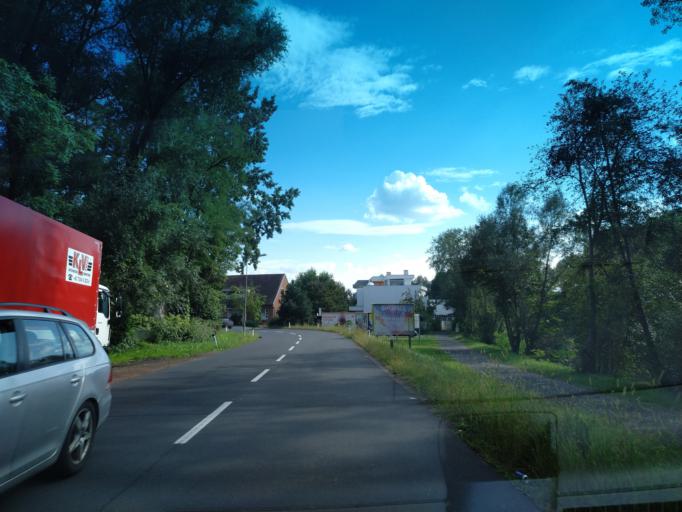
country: AT
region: Styria
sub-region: Politischer Bezirk Leibnitz
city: Kaindorf an der Sulm
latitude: 46.7935
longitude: 15.5321
